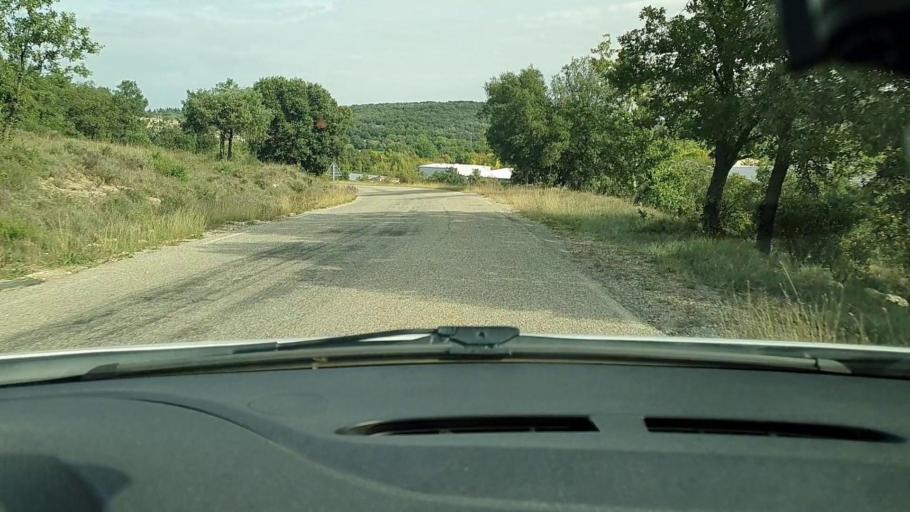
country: FR
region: Languedoc-Roussillon
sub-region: Departement du Gard
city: Saint-Quentin-la-Poterie
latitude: 44.1309
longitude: 4.4018
